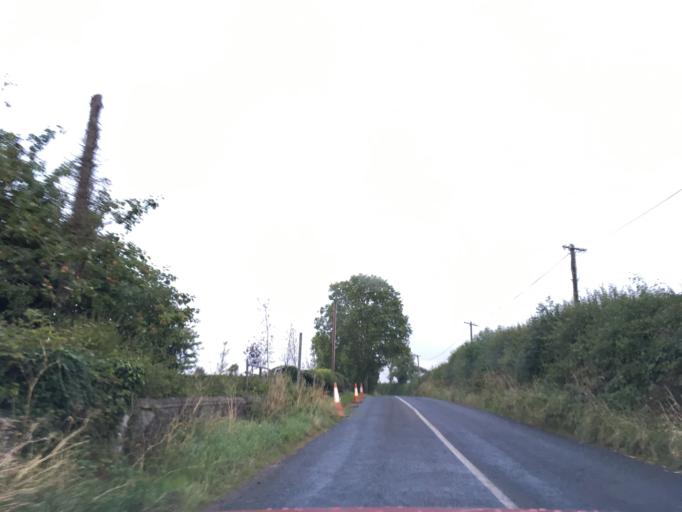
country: IE
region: Munster
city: Cahir
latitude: 52.4558
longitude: -7.9562
